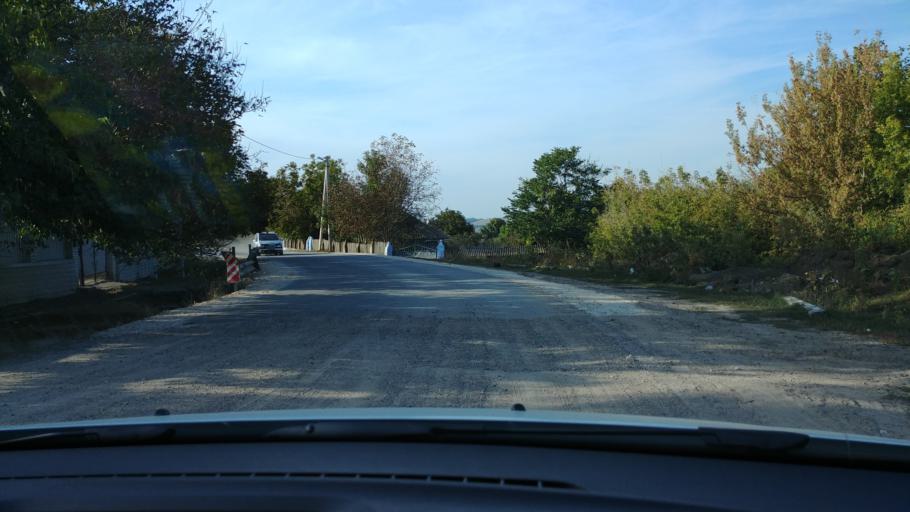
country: MD
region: Rezina
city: Rezina
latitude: 47.7486
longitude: 28.8844
